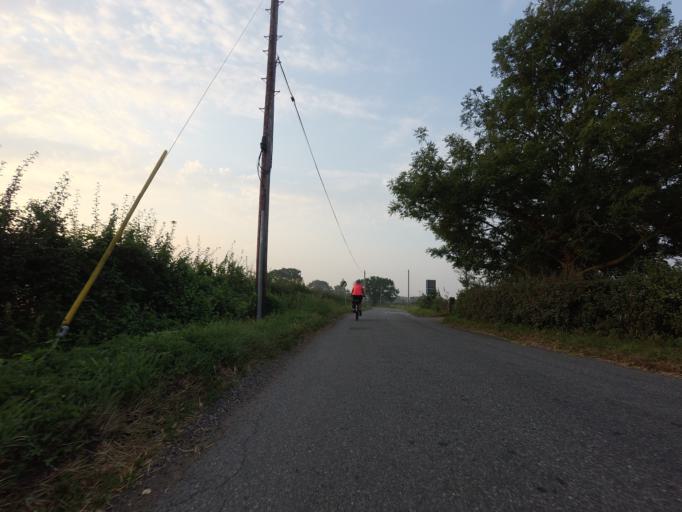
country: GB
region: England
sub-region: Kent
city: Lenham
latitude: 51.1858
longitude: 0.7155
